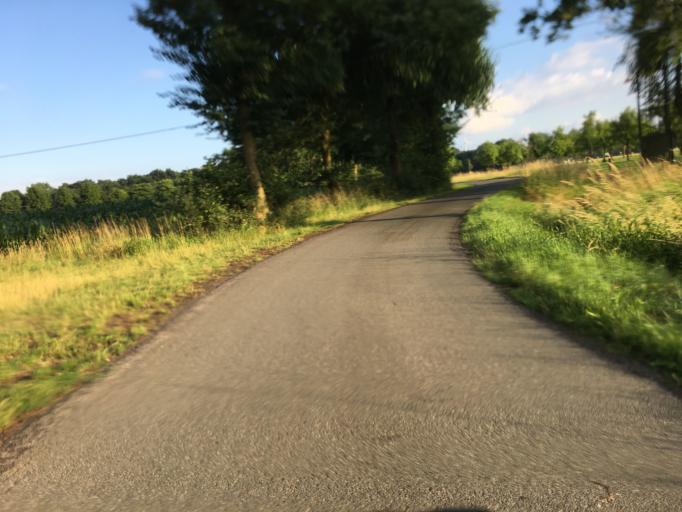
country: DE
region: North Rhine-Westphalia
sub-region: Regierungsbezirk Munster
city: Greven
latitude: 52.0524
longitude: 7.5604
